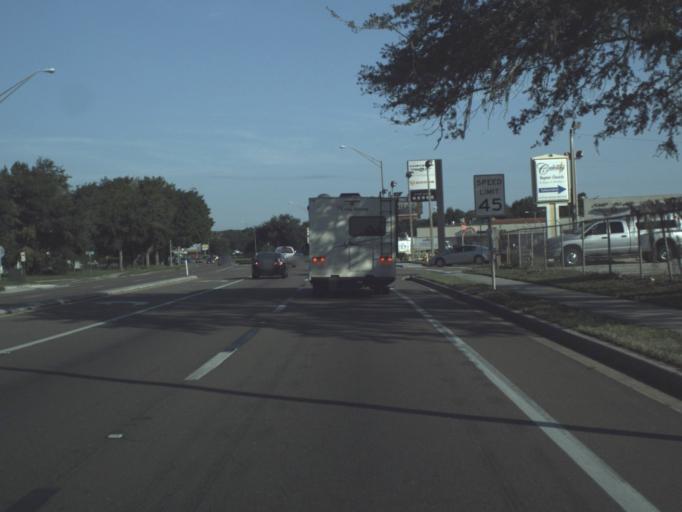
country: US
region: Florida
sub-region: Polk County
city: Lakeland
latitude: 28.0728
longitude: -81.9583
